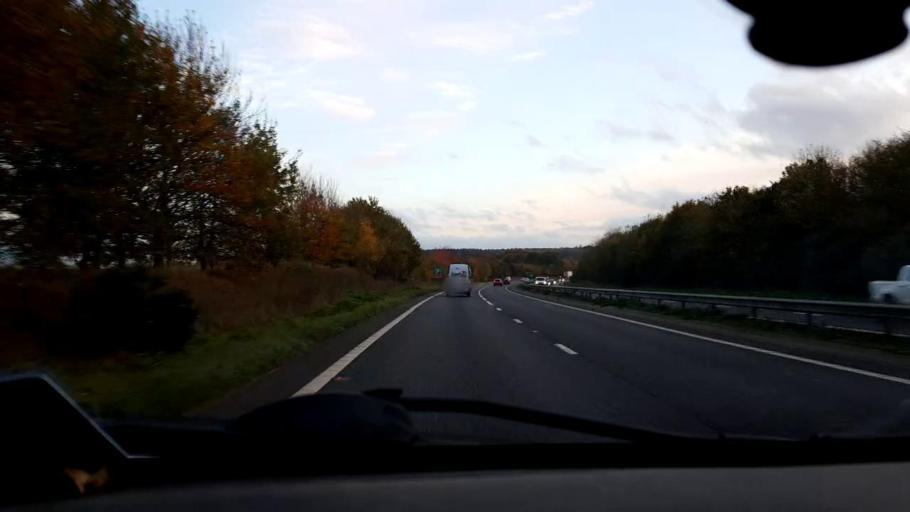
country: GB
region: England
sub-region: Norfolk
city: Bowthorpe
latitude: 52.6392
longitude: 1.1945
